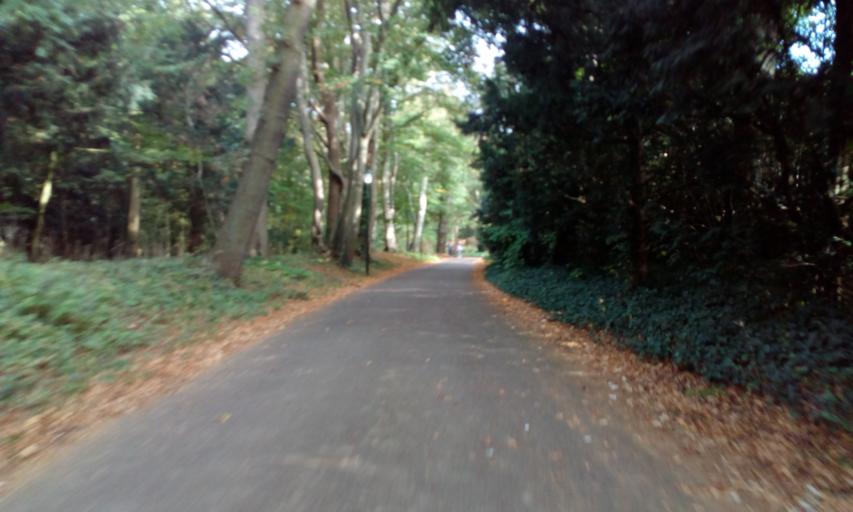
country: NL
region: South Holland
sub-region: Gemeente Wassenaar
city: Wassenaar
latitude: 52.1191
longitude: 4.3751
